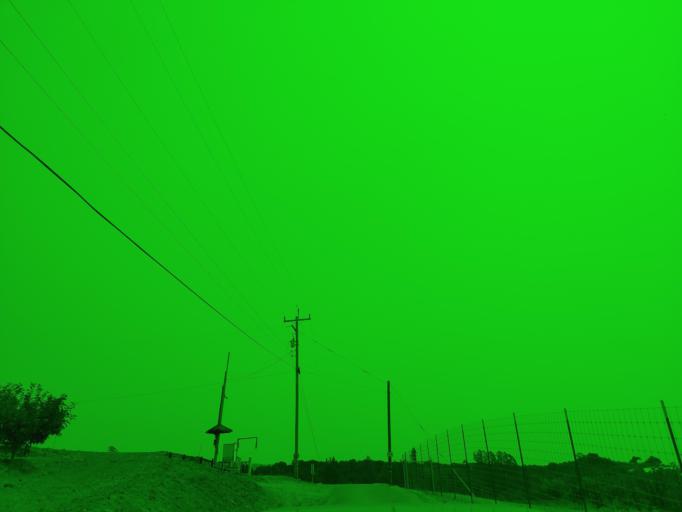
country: US
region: California
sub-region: Santa Cruz County
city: Corralitos
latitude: 36.9922
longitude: -121.7806
